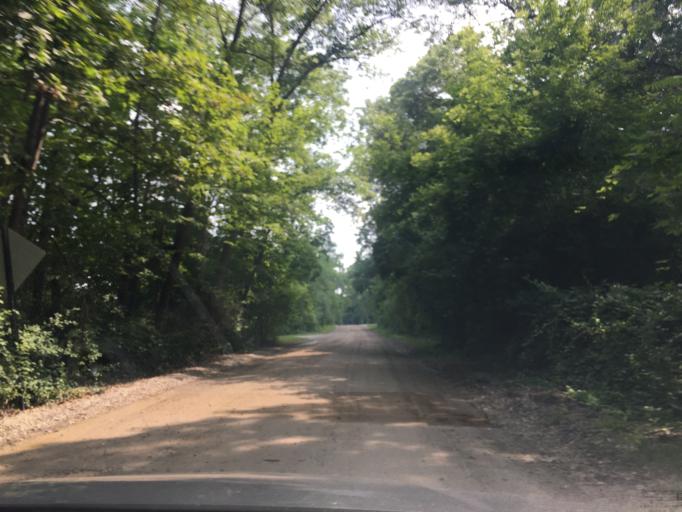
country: US
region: Michigan
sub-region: Oakland County
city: Bloomfield Hills
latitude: 42.5807
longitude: -83.2318
